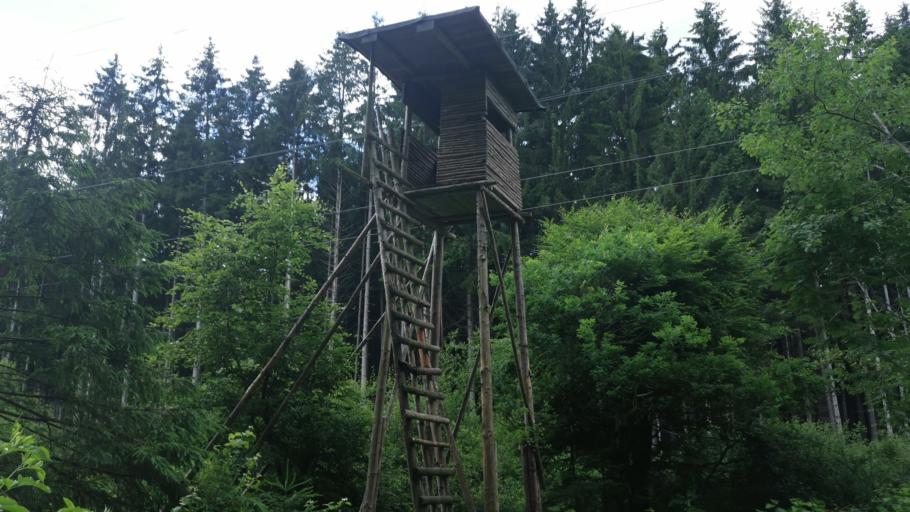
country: DE
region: Bavaria
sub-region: Upper Bavaria
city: Schaftlarn
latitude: 48.0084
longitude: 11.4598
